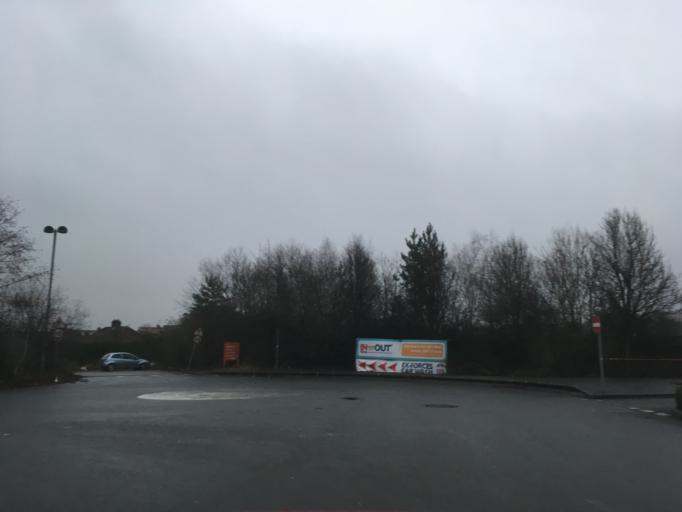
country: GB
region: Wales
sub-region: Cardiff
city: Radyr
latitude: 51.4670
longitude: -3.2668
